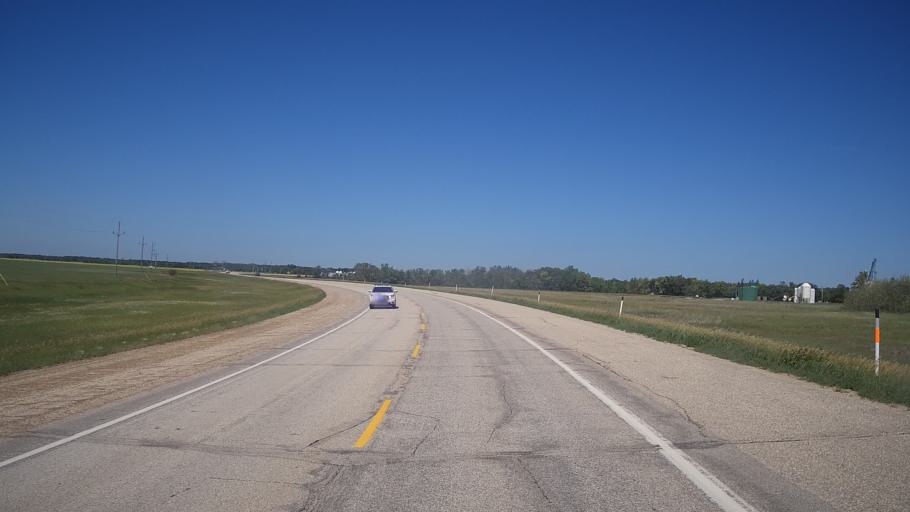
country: CA
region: Manitoba
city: Portage la Prairie
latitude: 50.1257
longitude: -98.5712
